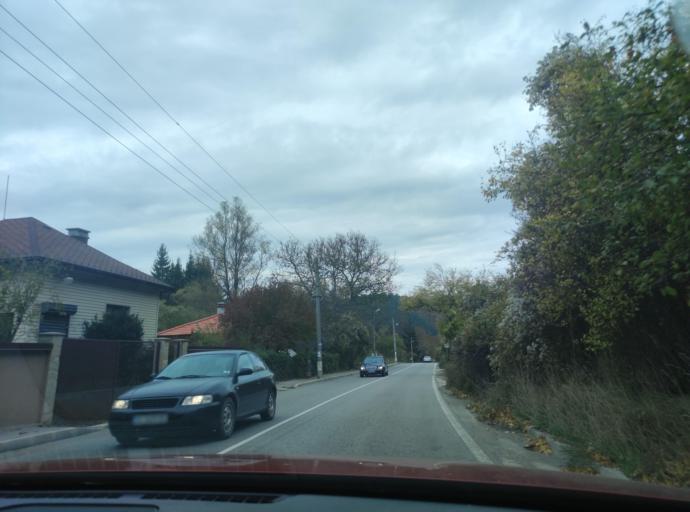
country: BG
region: Sofiya
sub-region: Obshtina Godech
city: Godech
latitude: 42.9711
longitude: 23.1419
